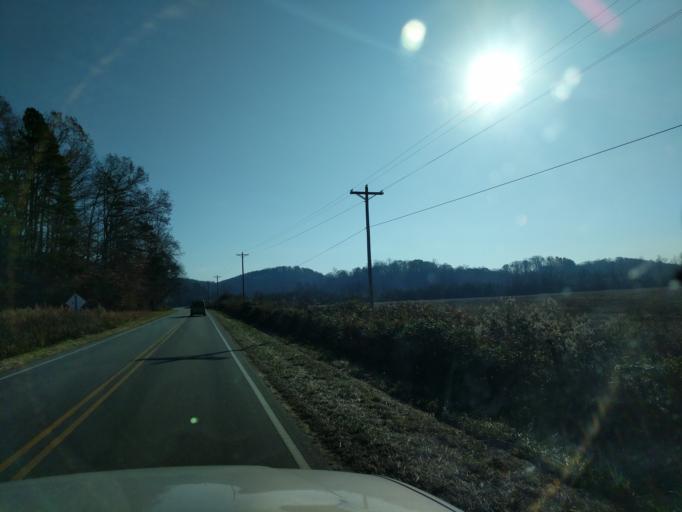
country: US
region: North Carolina
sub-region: Rutherford County
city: Rutherfordton
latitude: 35.2856
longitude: -82.0266
